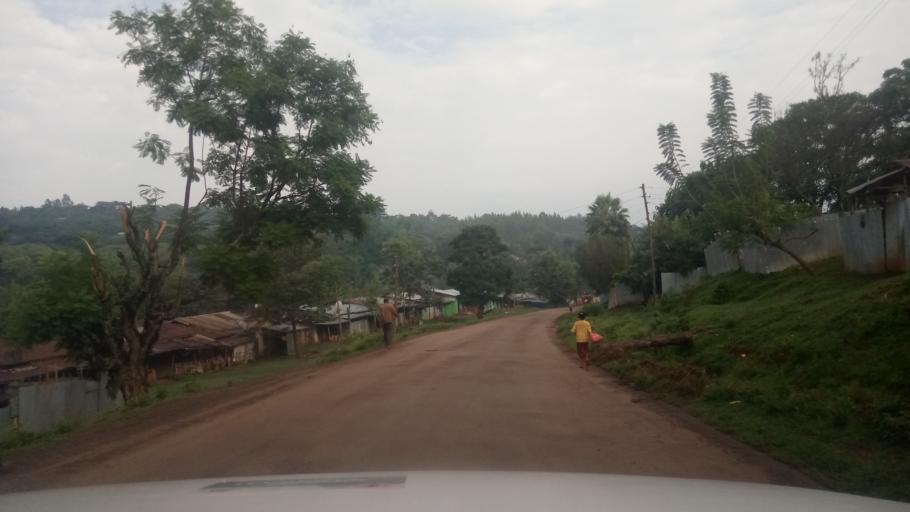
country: ET
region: Oromiya
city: Agaro
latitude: 7.8380
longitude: 36.6666
